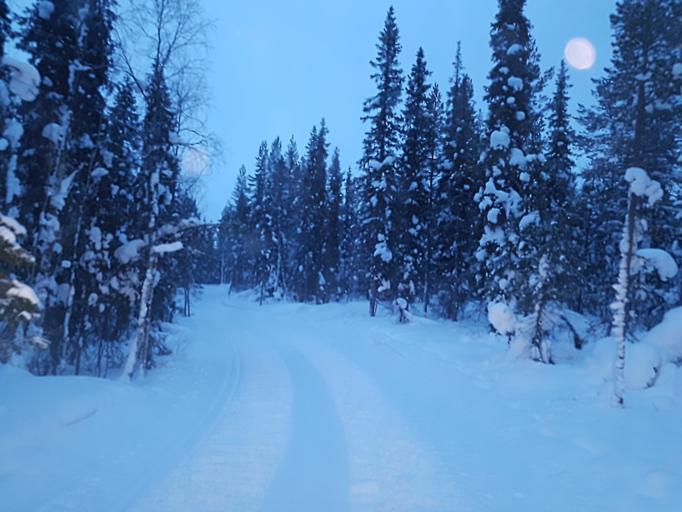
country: FI
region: Lapland
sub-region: Tunturi-Lappi
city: Kolari
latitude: 67.6179
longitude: 24.1674
